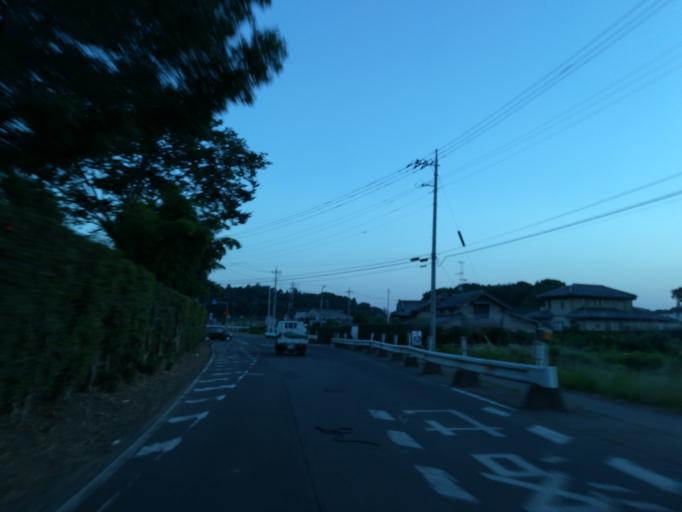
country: JP
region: Ibaraki
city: Makabe
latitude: 36.2892
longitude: 140.0594
